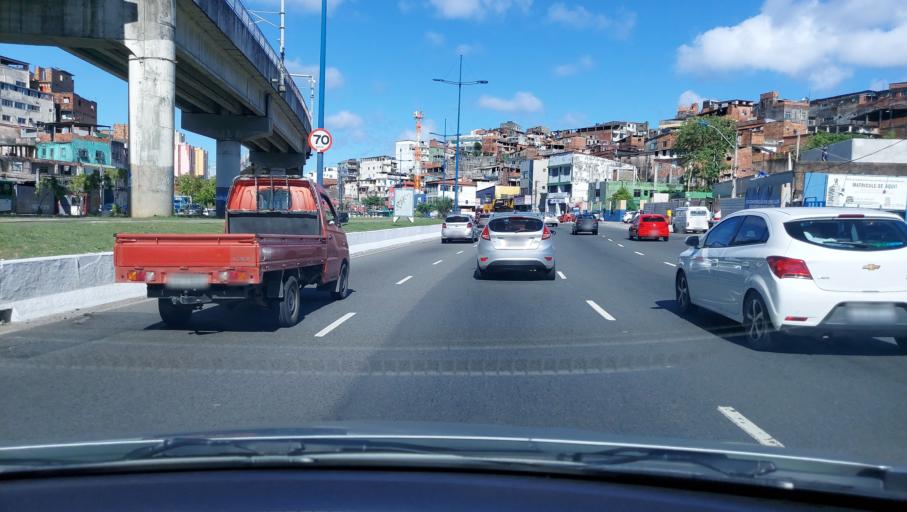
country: BR
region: Bahia
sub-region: Salvador
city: Salvador
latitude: -12.9843
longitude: -38.4864
